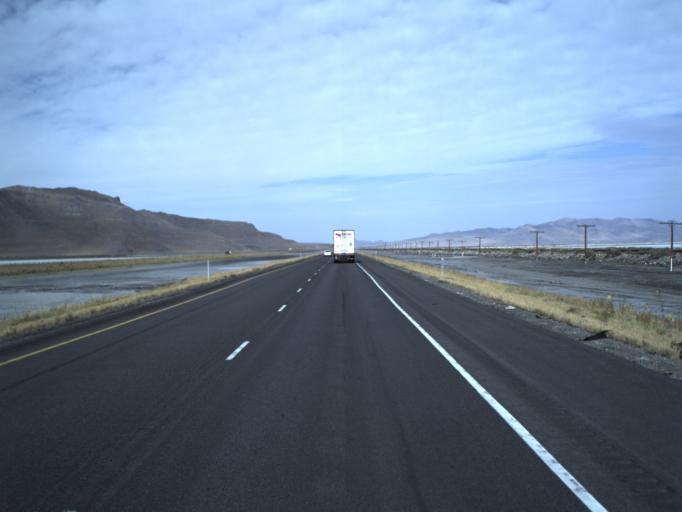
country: US
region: Utah
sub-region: Tooele County
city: Grantsville
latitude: 40.7227
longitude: -112.5620
